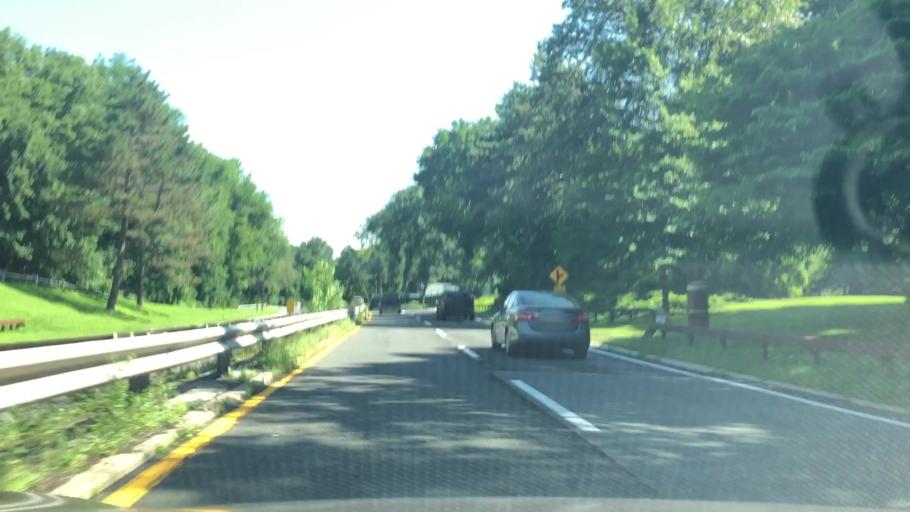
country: US
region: New York
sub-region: Westchester County
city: Hartsdale
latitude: 41.0113
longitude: -73.7943
